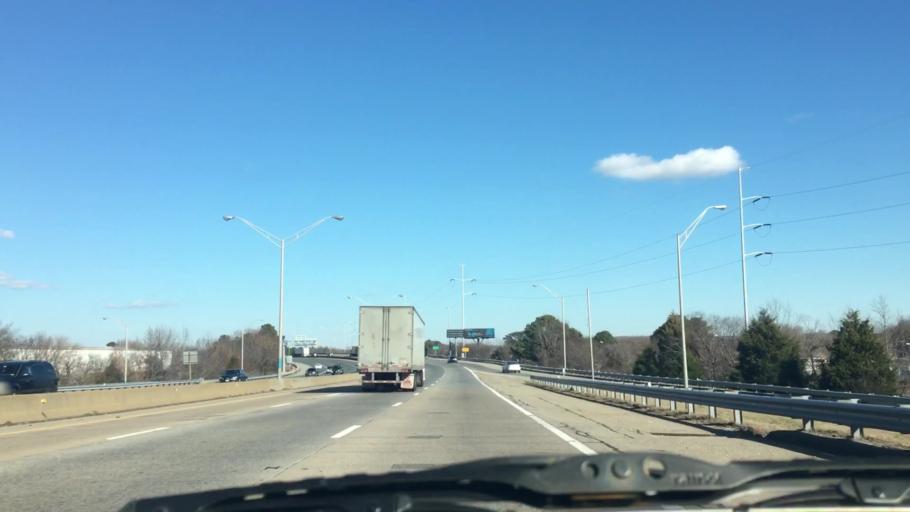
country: US
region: Virginia
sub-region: City of Newport News
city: Newport News
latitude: 36.9960
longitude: -76.4083
